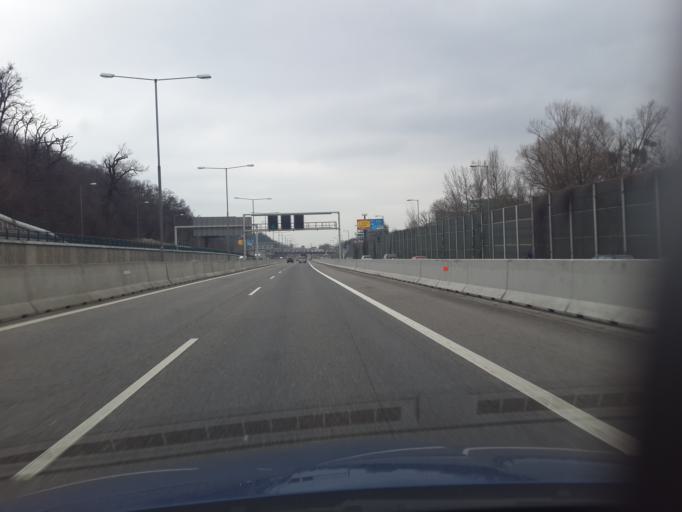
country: SK
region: Bratislavsky
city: Bratislava
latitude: 48.1593
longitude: 17.0762
